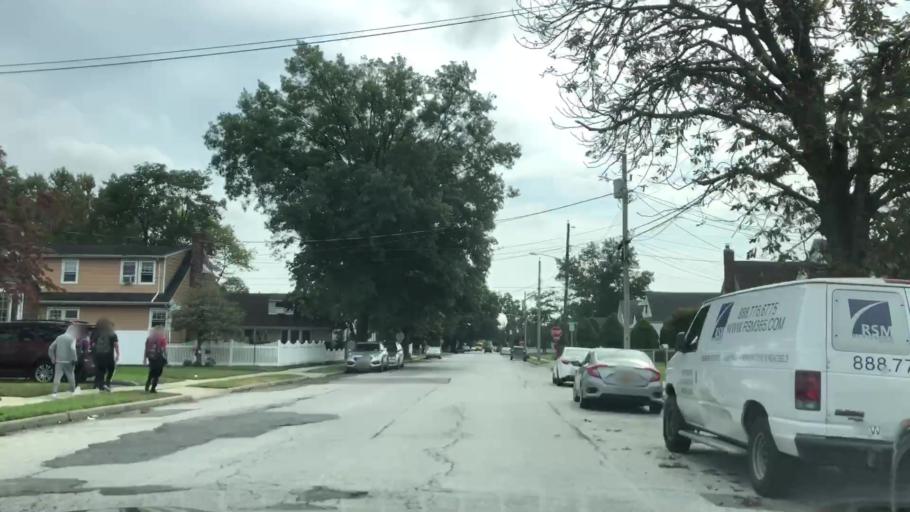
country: US
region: New York
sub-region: Nassau County
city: South Floral Park
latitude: 40.7125
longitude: -73.6931
